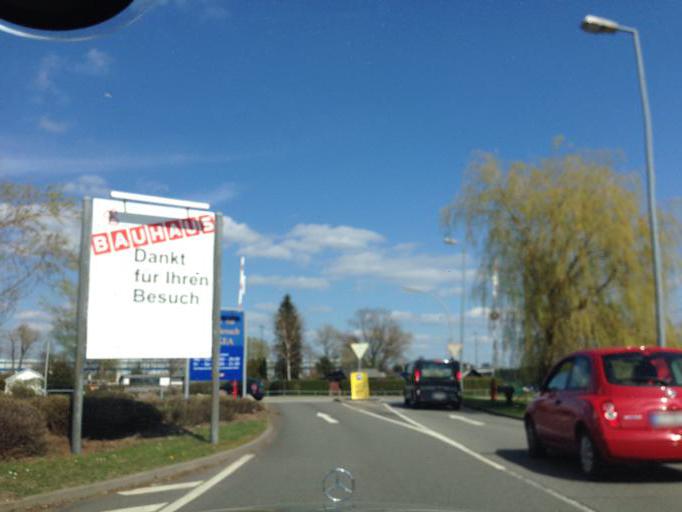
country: DE
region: Hamburg
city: Wandsbek
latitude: 53.5103
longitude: 10.0966
